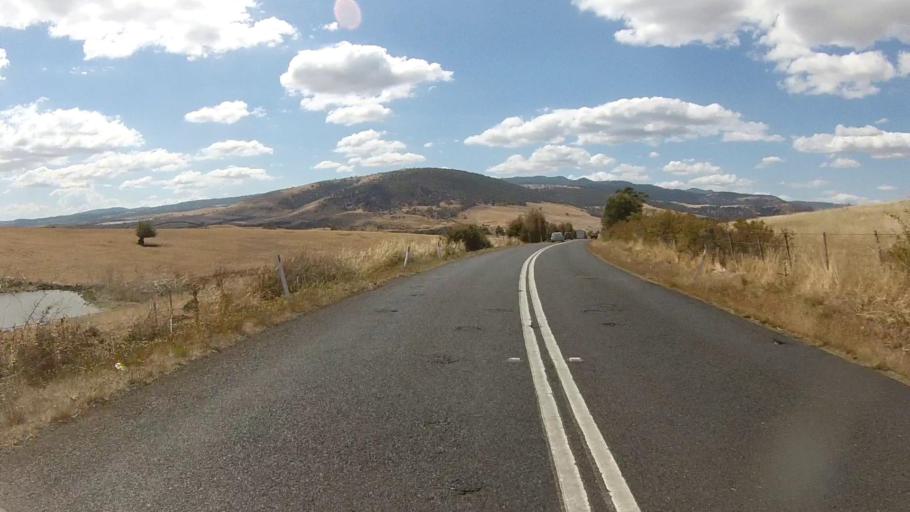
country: AU
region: Tasmania
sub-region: Derwent Valley
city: New Norfolk
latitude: -42.7365
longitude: 146.9366
